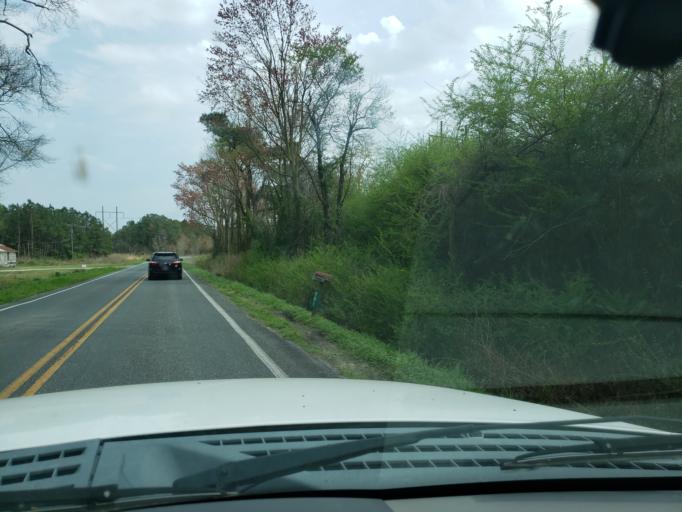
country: US
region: North Carolina
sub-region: Duplin County
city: Beulaville
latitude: 34.7740
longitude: -77.8116
